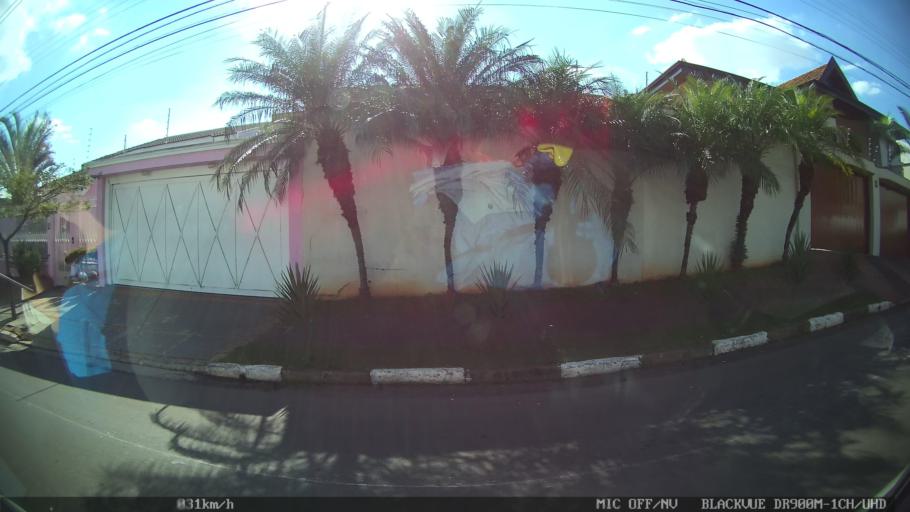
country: BR
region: Sao Paulo
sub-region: Sumare
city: Sumare
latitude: -22.8233
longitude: -47.2800
